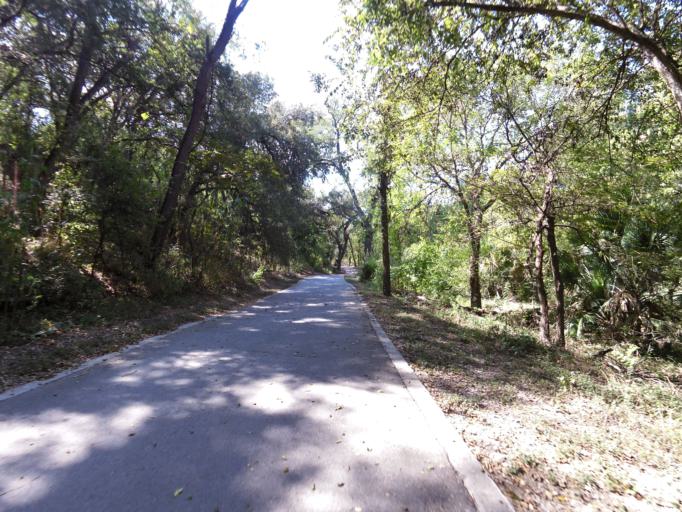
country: US
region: Texas
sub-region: Bexar County
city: China Grove
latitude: 29.3912
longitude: -98.4158
